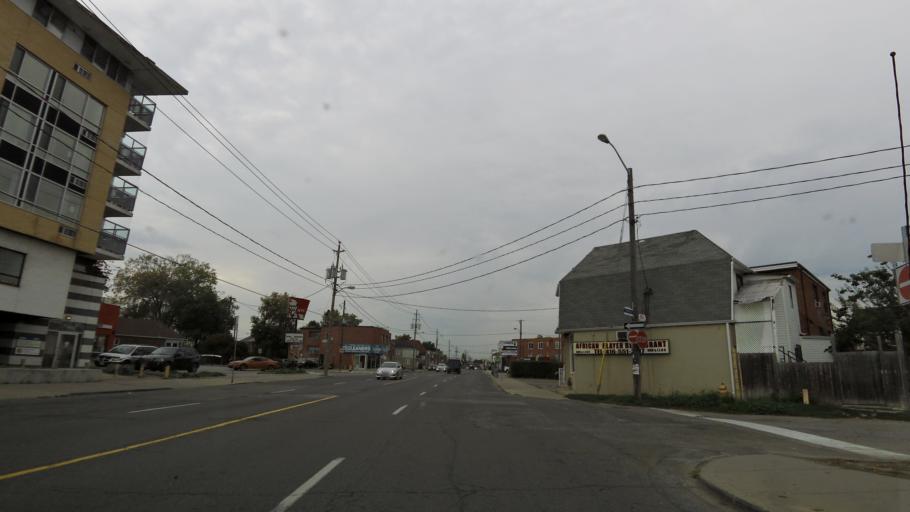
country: CA
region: Ontario
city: Etobicoke
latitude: 43.6891
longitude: -79.4957
